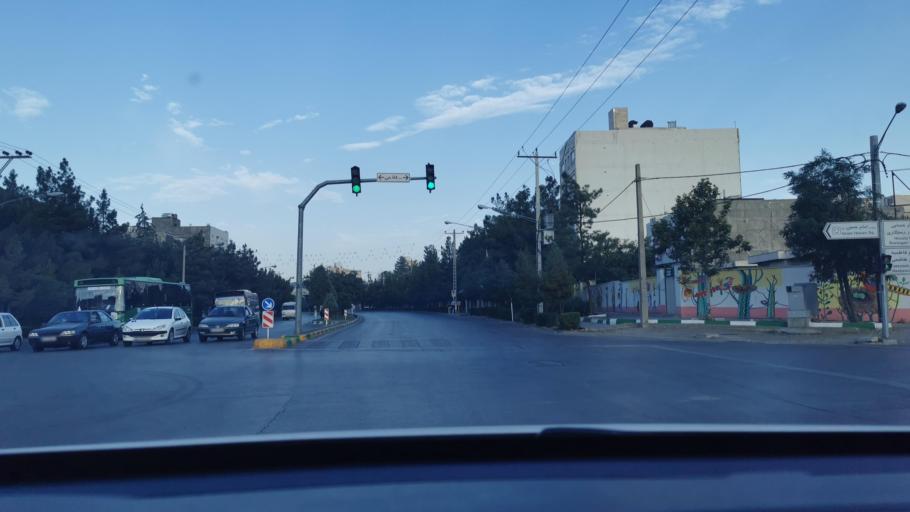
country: IR
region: Razavi Khorasan
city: Mashhad
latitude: 36.3593
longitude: 59.5076
